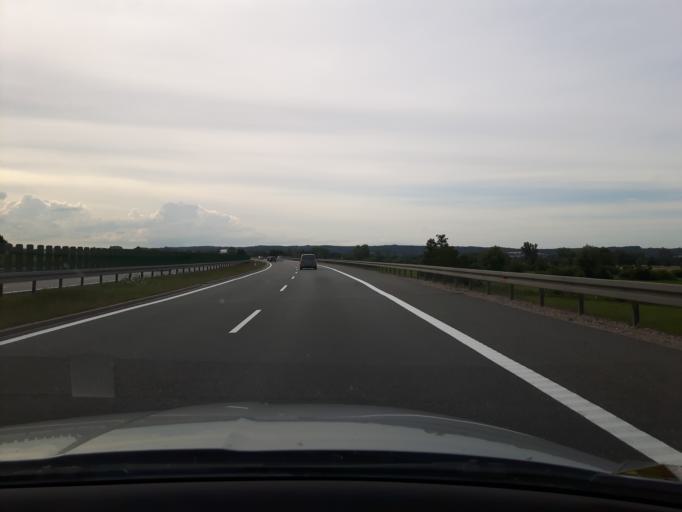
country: PL
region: Warmian-Masurian Voivodeship
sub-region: Powiat elblaski
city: Paslek
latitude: 54.0891
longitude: 19.5967
